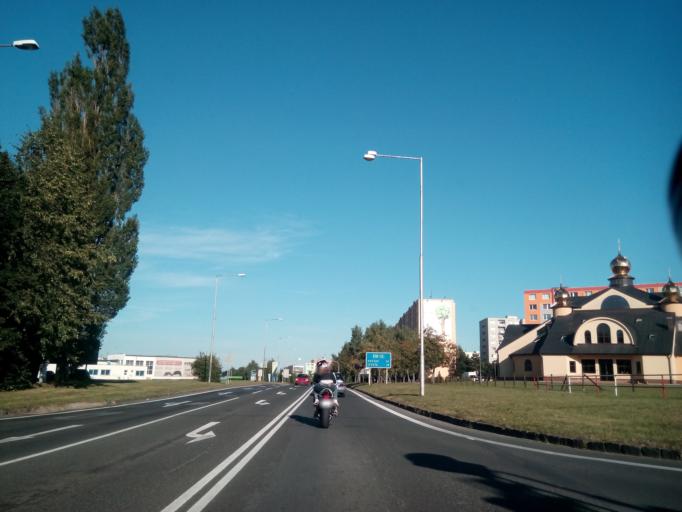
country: SK
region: Presovsky
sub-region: Okres Poprad
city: Poprad
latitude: 49.0512
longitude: 20.2953
